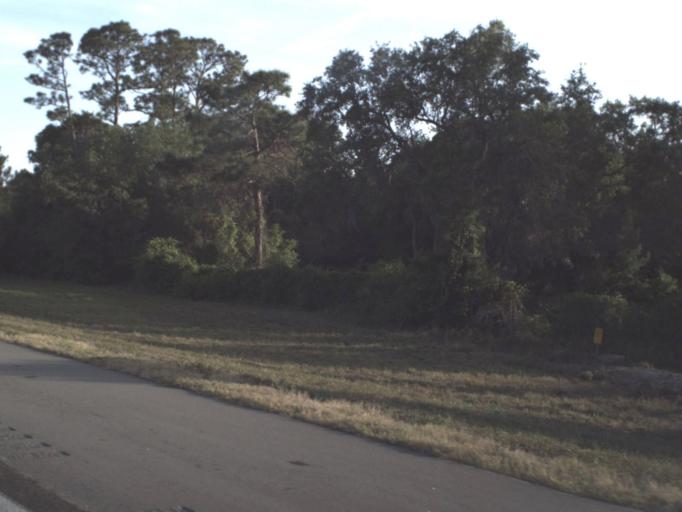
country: US
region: Florida
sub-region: Brevard County
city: Mims
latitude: 28.7154
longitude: -80.8901
